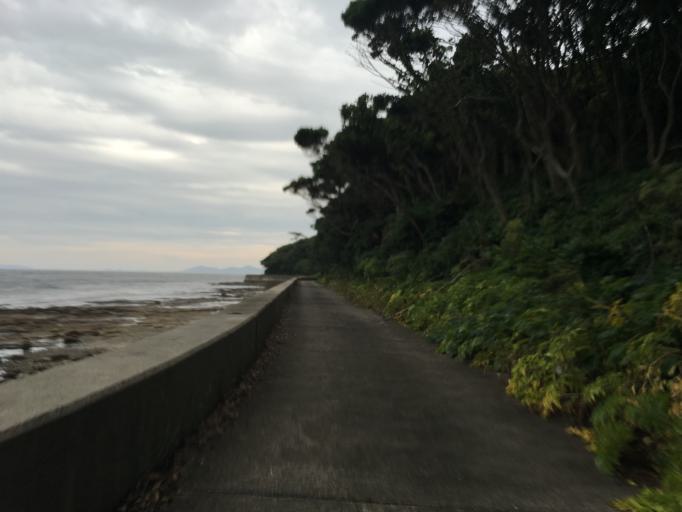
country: JP
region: Aichi
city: Ishiki
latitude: 34.7314
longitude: 137.0428
